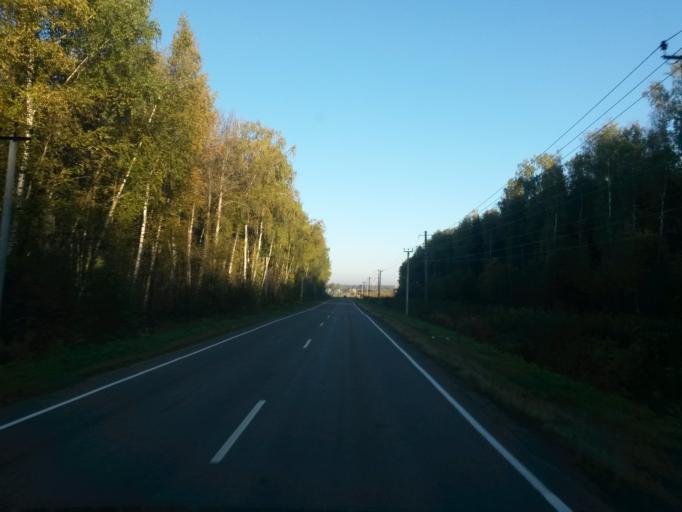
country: RU
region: Moskovskaya
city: Belyye Stolby
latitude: 55.2562
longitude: 37.7773
